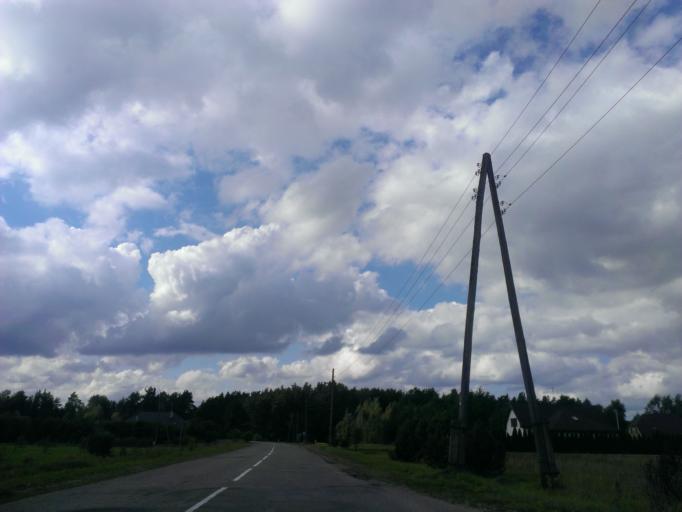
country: LV
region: Garkalne
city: Garkalne
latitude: 56.9658
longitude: 24.5032
